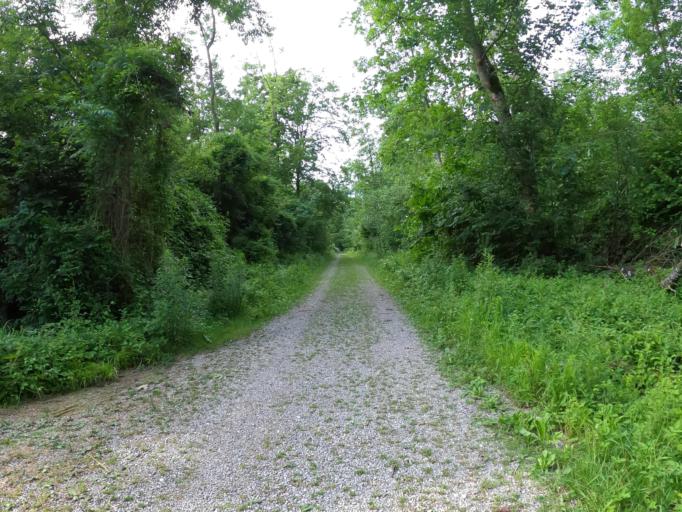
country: DE
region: Bavaria
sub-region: Swabia
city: Nersingen
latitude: 48.4483
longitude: 10.1548
